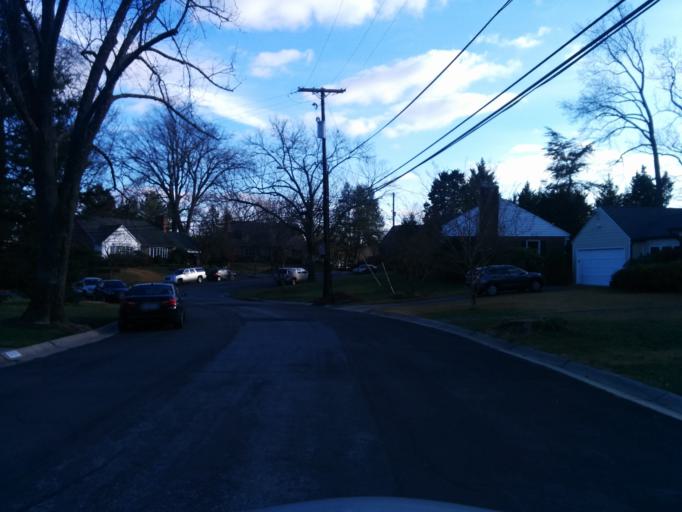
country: US
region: Maryland
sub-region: Montgomery County
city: Brookmont
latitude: 38.9563
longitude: -77.1198
